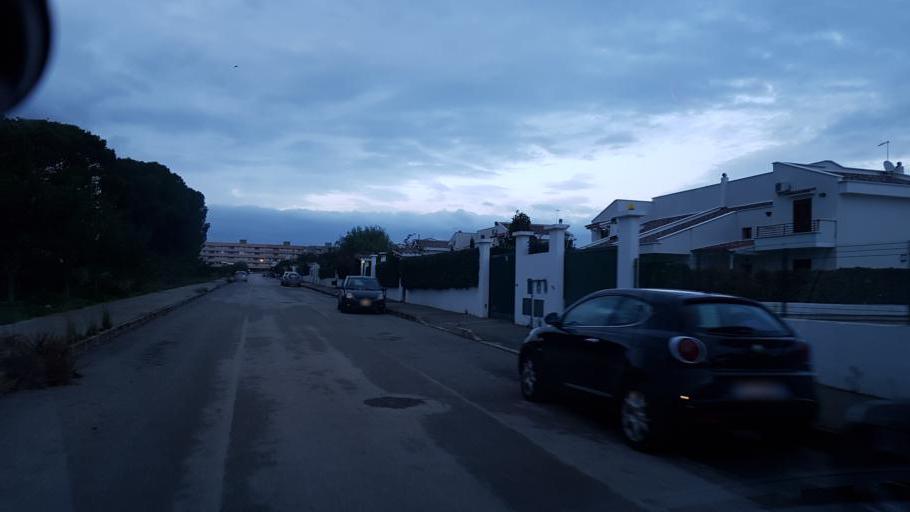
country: IT
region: Apulia
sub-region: Provincia di Taranto
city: Paolo VI
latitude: 40.5276
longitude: 17.2847
